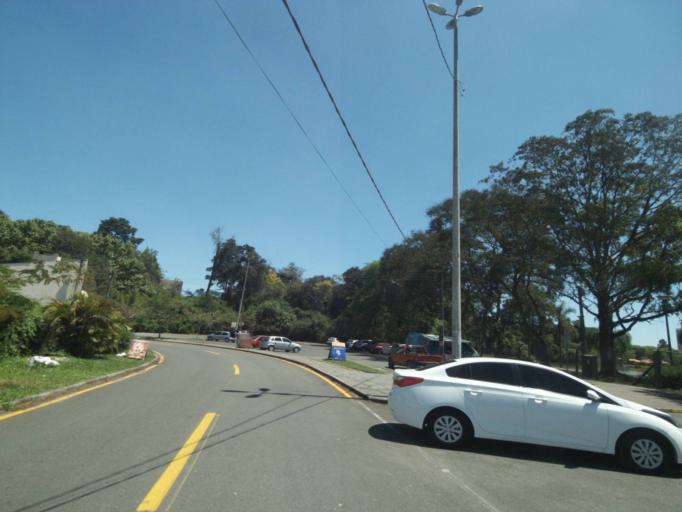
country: BR
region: Parana
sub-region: Curitiba
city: Curitiba
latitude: -25.3918
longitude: -49.2282
